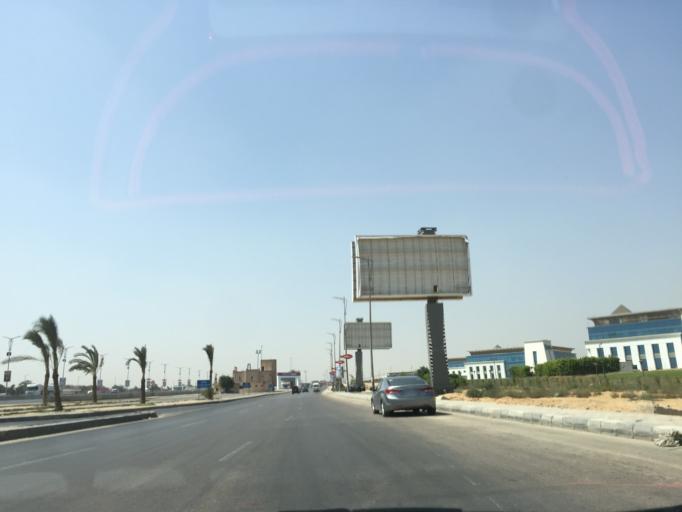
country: EG
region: Al Jizah
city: Awsim
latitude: 30.0646
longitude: 31.0238
